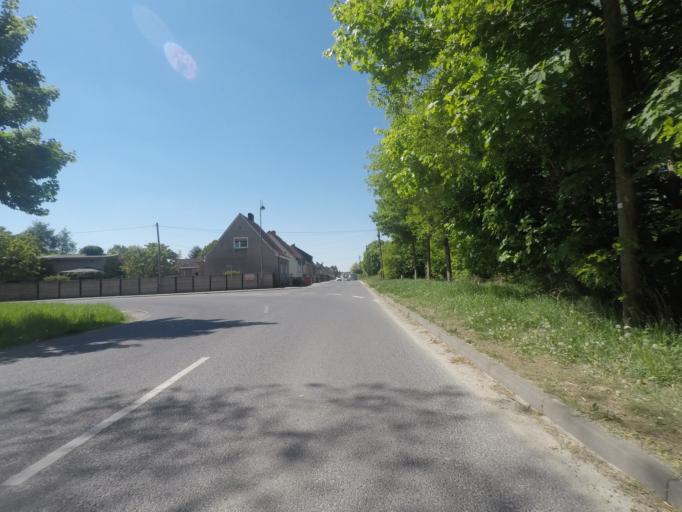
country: DE
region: Brandenburg
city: Melchow
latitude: 52.8516
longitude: 13.7007
